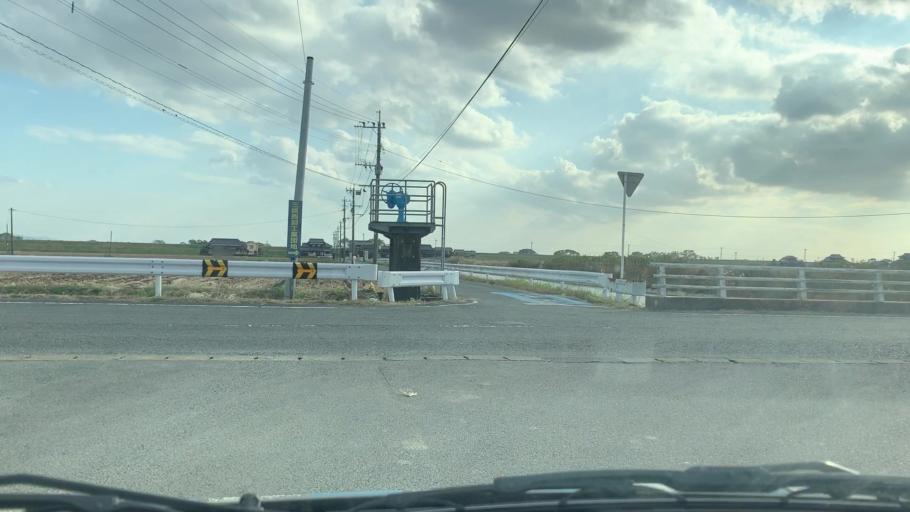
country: JP
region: Saga Prefecture
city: Kanzakimachi-kanzaki
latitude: 33.2795
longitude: 130.4415
